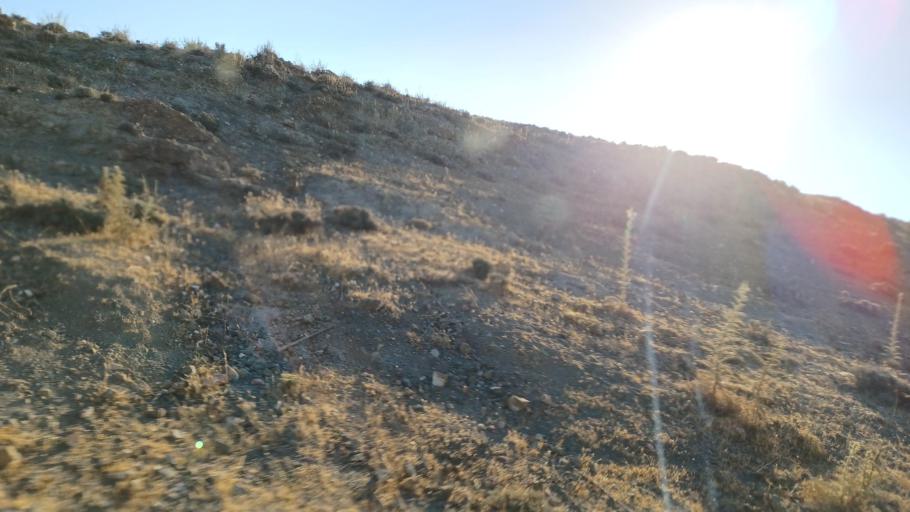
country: CY
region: Larnaka
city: Troulloi
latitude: 35.0048
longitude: 33.6205
